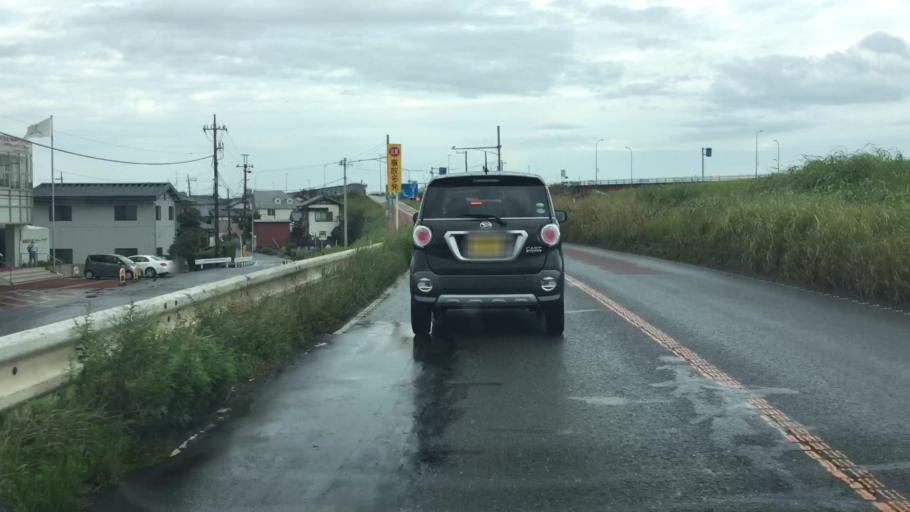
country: JP
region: Ibaraki
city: Toride
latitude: 35.8851
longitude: 140.0540
